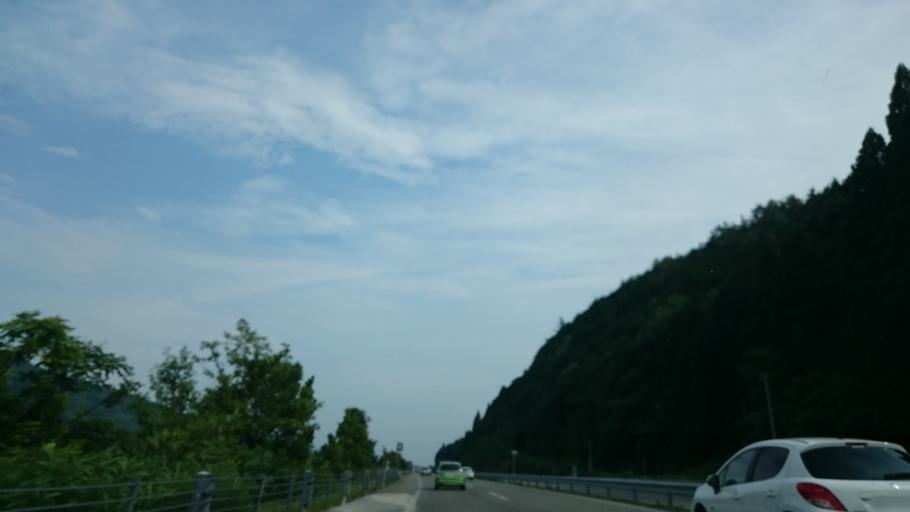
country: JP
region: Gifu
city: Gujo
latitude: 35.8454
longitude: 136.8729
